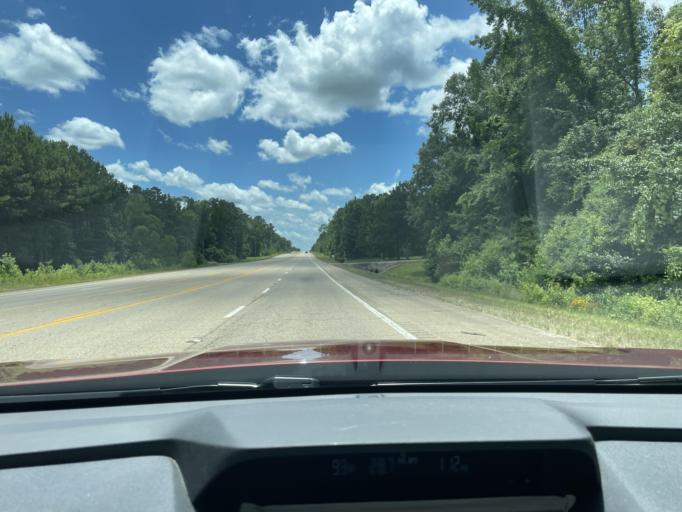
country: US
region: Arkansas
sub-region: Drew County
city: Monticello
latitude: 33.6956
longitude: -91.8067
